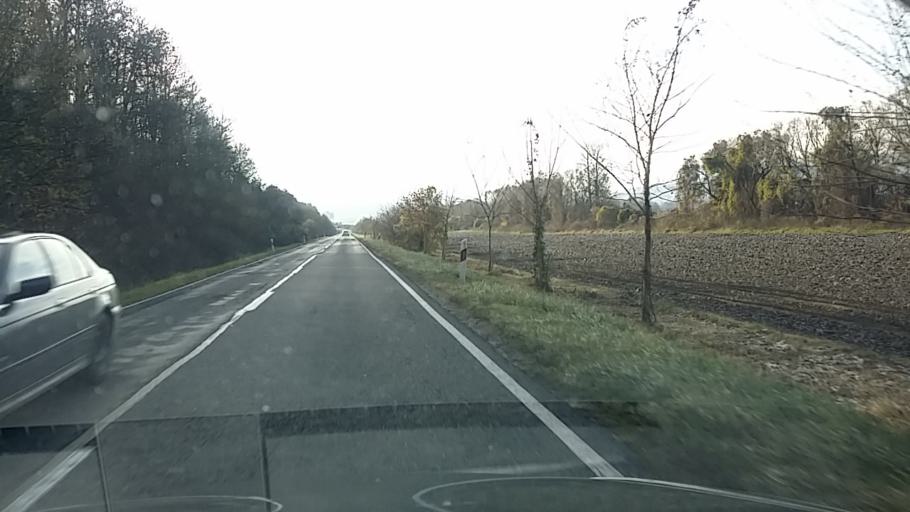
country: HU
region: Veszprem
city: Urkut
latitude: 46.9846
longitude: 17.6295
